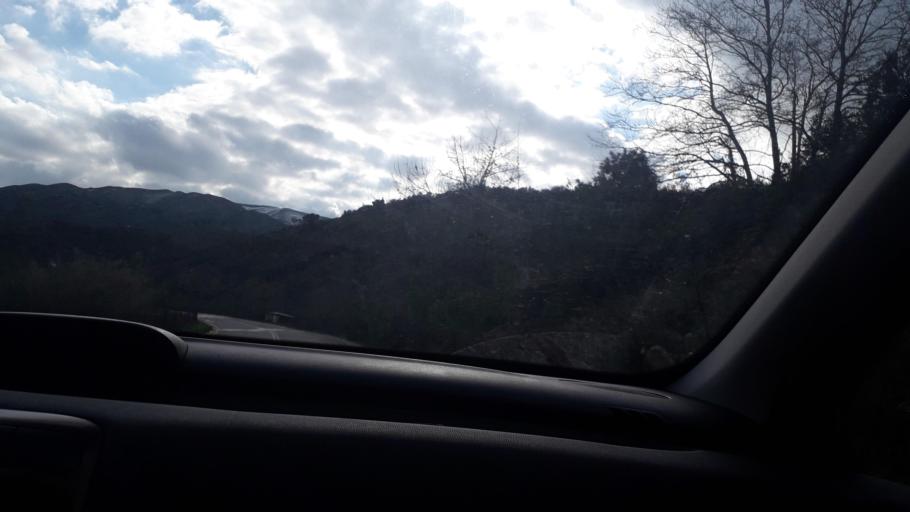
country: GR
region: Crete
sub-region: Nomos Rethymnis
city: Agia Foteini
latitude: 35.2845
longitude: 24.5625
